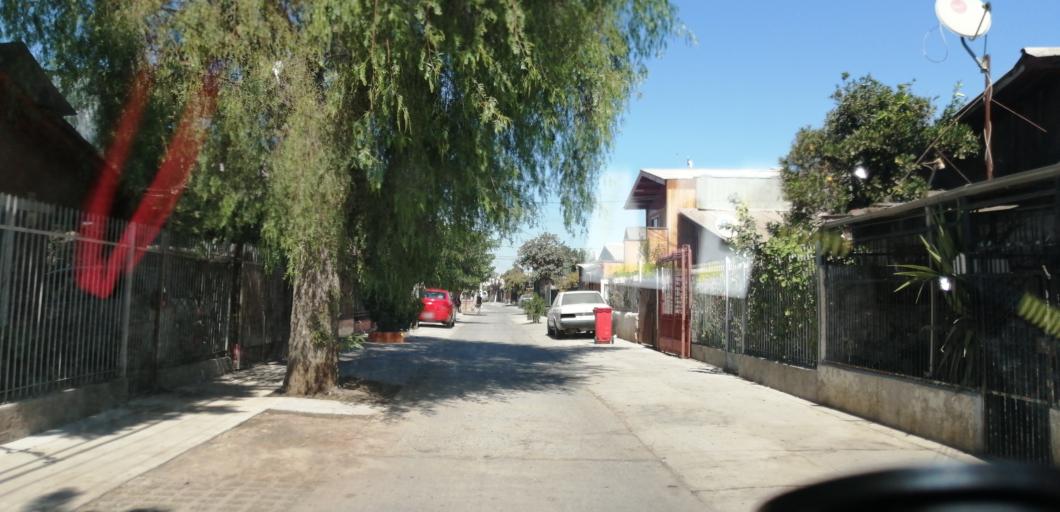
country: CL
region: Santiago Metropolitan
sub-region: Provincia de Santiago
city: Lo Prado
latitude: -33.4326
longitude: -70.7555
